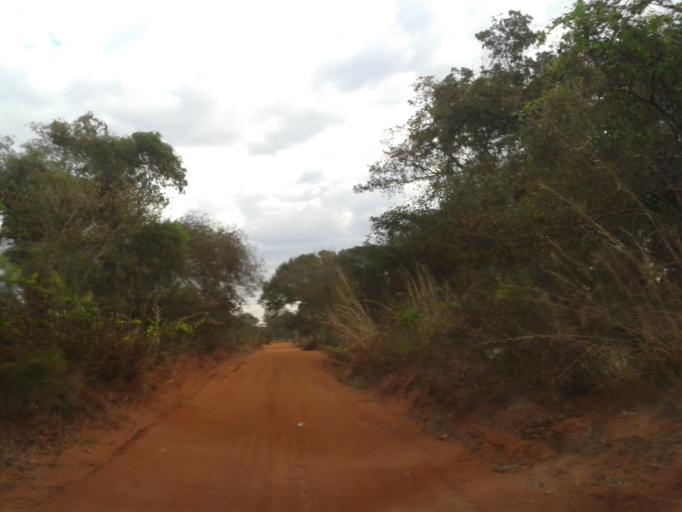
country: BR
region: Minas Gerais
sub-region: Santa Vitoria
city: Santa Vitoria
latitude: -18.7677
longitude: -50.1875
